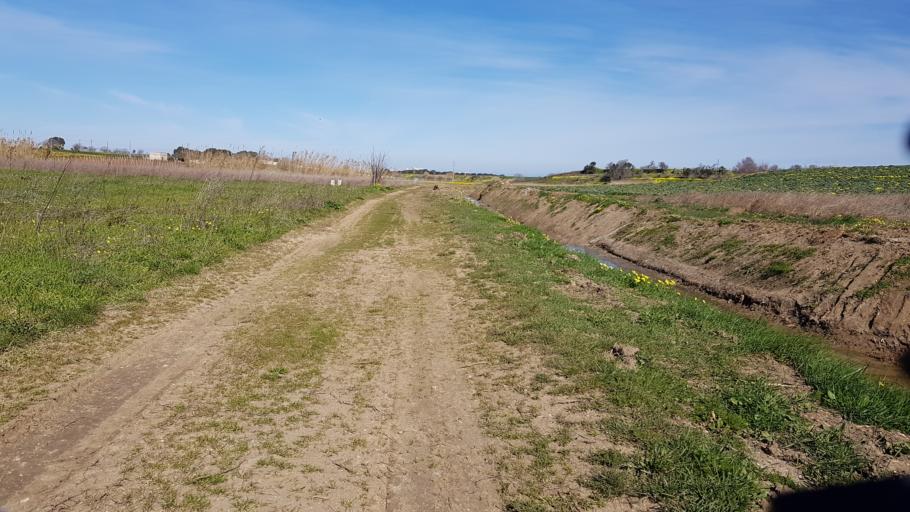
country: IT
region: Apulia
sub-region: Provincia di Brindisi
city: La Rosa
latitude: 40.6005
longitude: 17.9298
